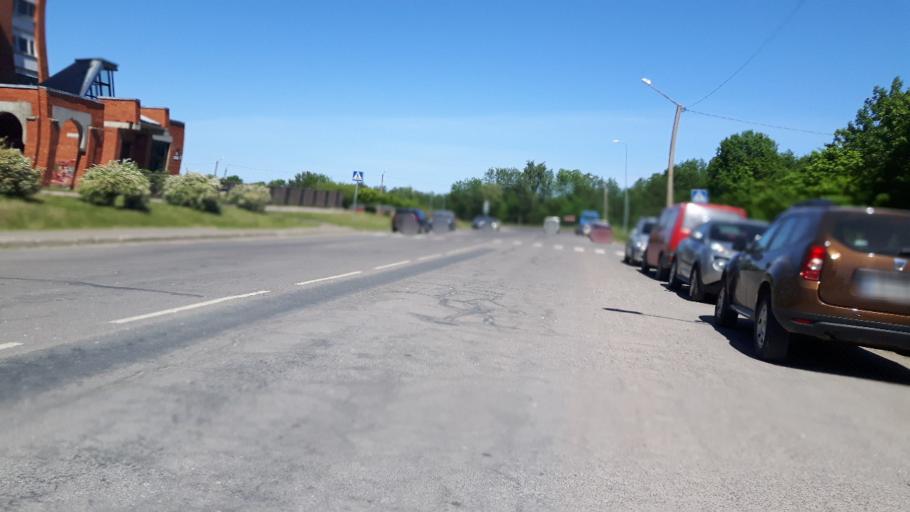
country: EE
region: Ida-Virumaa
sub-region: Sillamaee linn
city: Sillamae
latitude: 59.3929
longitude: 27.7972
